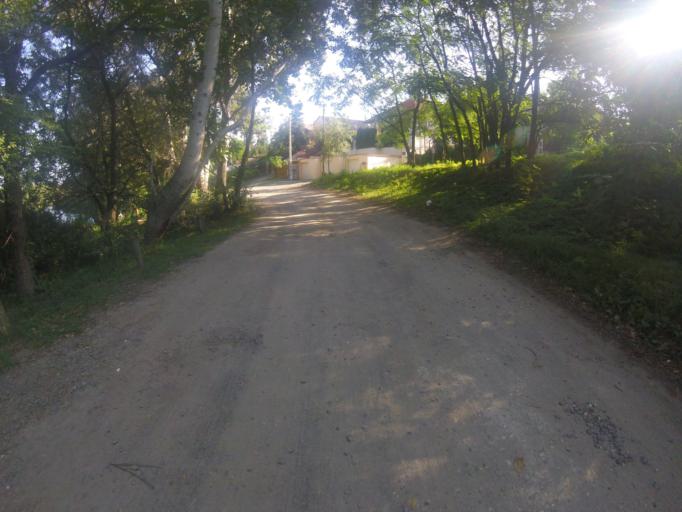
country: HU
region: Pest
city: Veresegyhaz
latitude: 47.6467
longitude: 19.2803
